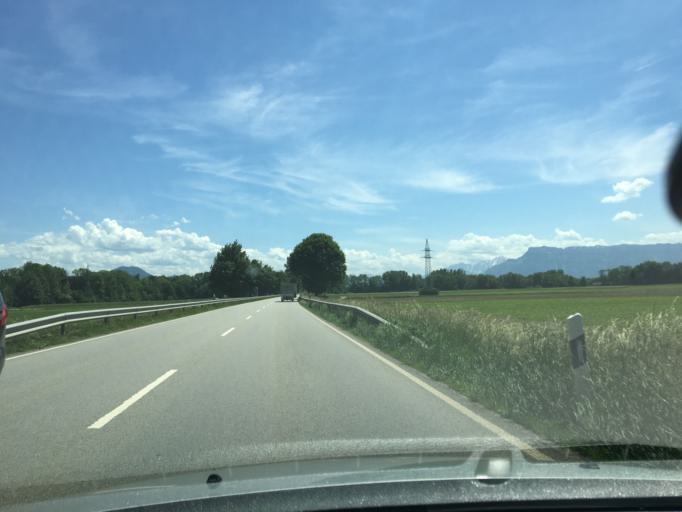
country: DE
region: Bavaria
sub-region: Upper Bavaria
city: Laufen
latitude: 47.8917
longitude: 12.9609
